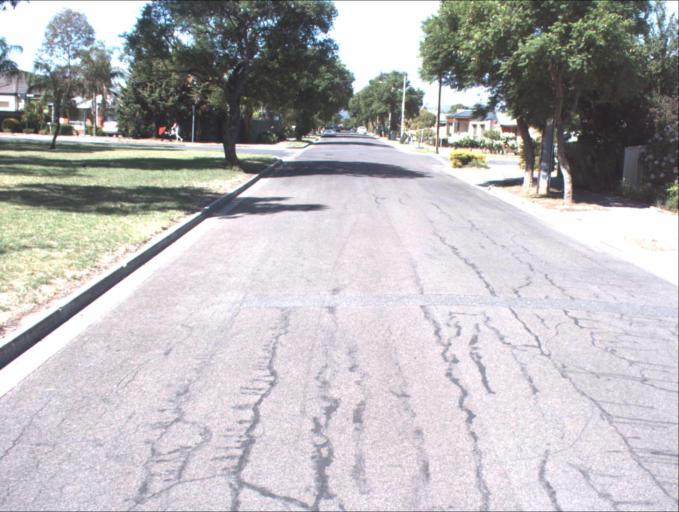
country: AU
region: South Australia
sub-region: Port Adelaide Enfield
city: Gilles Plains
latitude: -34.8609
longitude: 138.6413
